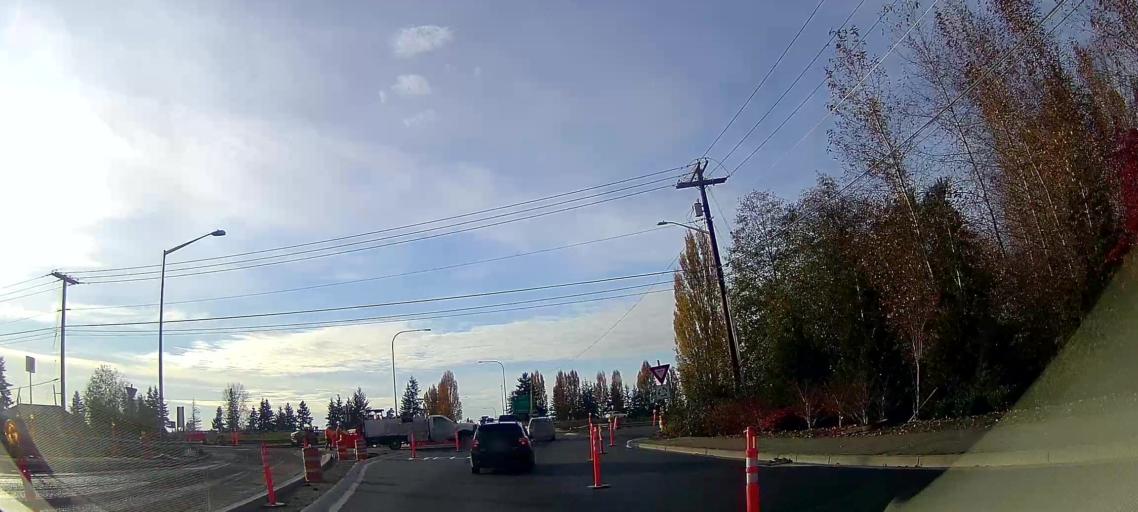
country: US
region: Washington
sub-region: Skagit County
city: Mount Vernon
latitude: 48.3995
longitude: -122.3275
